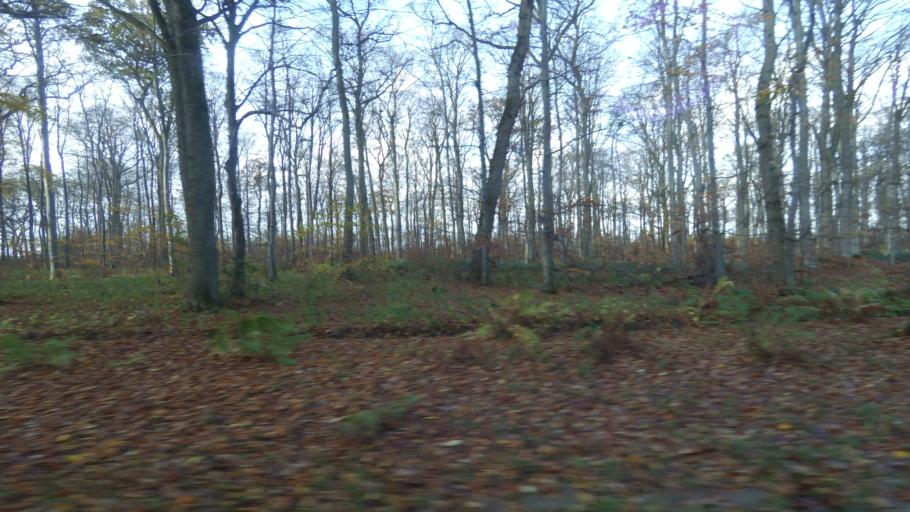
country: DK
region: Central Jutland
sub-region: Odder Kommune
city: Odder
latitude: 55.8576
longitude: 10.1615
